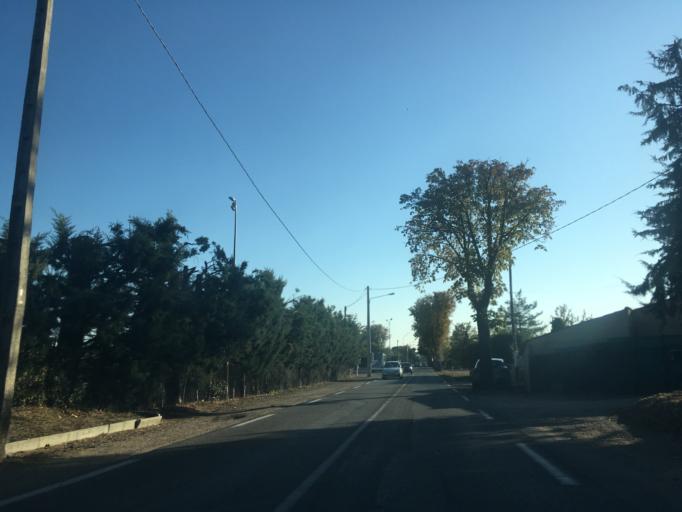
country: FR
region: Provence-Alpes-Cote d'Azur
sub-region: Departement du Var
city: Aups
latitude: 43.6222
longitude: 6.2221
